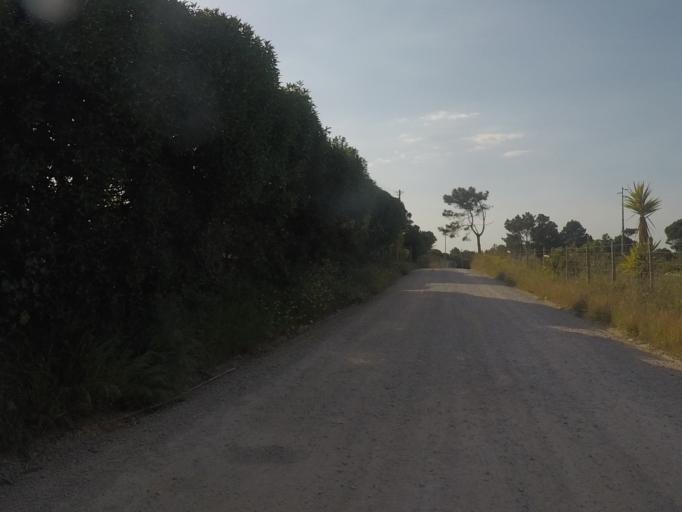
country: PT
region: Setubal
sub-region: Sesimbra
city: Sesimbra
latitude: 38.4410
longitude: -9.1943
